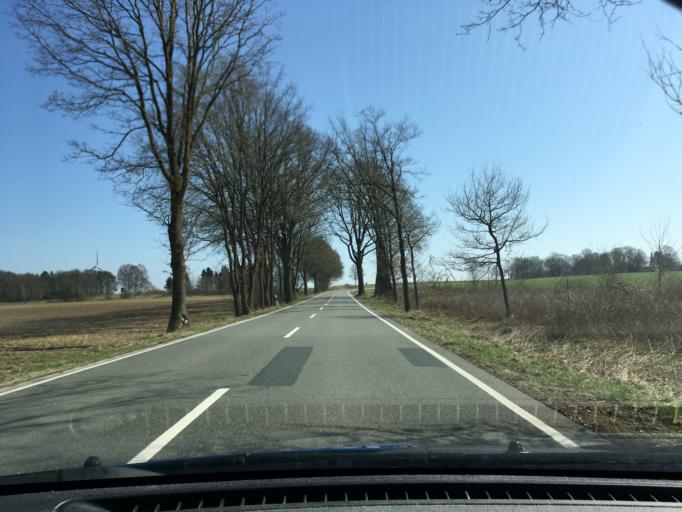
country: DE
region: Lower Saxony
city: Rehlingen
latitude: 53.1057
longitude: 10.2569
